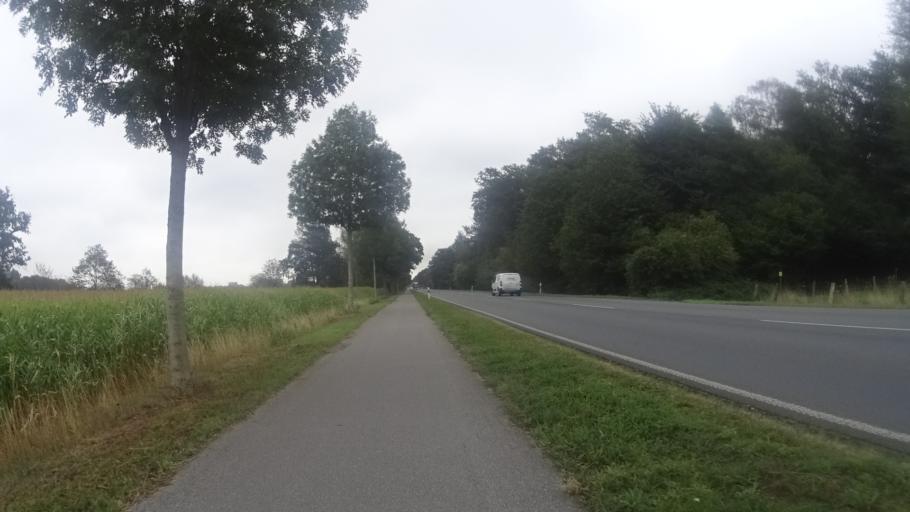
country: DE
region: North Rhine-Westphalia
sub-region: Regierungsbezirk Dusseldorf
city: Issum
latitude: 51.5251
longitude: 6.3789
